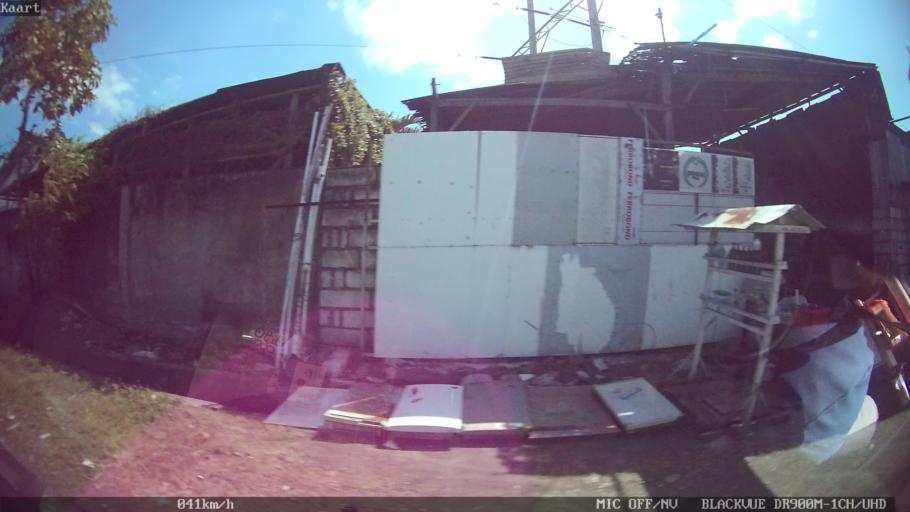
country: ID
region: Bali
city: Banjar Kertasari
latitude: -8.6393
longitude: 115.1792
